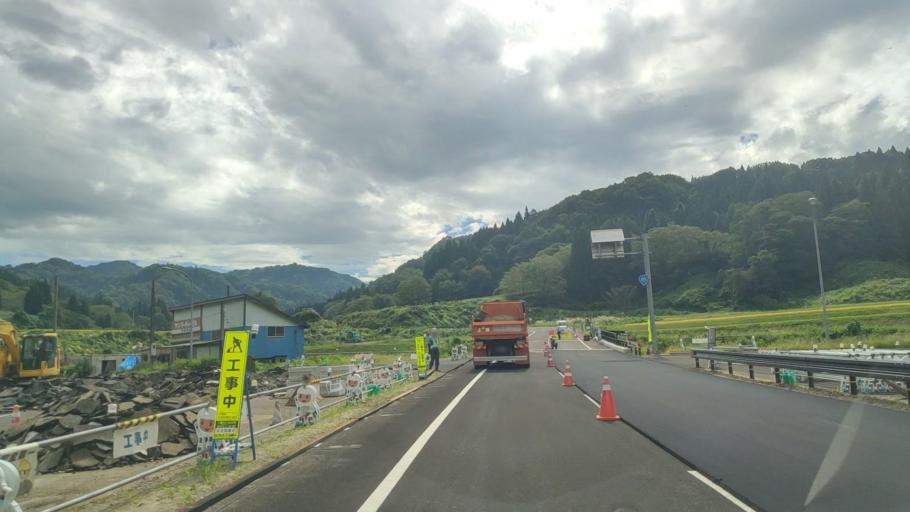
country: JP
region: Niigata
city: Arai
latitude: 36.9504
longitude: 138.2807
